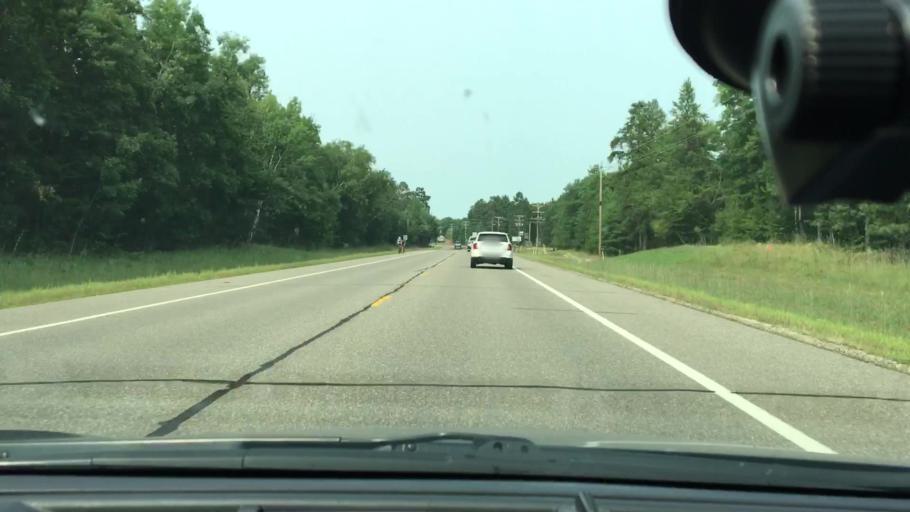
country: US
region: Minnesota
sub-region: Crow Wing County
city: Cross Lake
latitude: 46.5706
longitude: -94.1291
